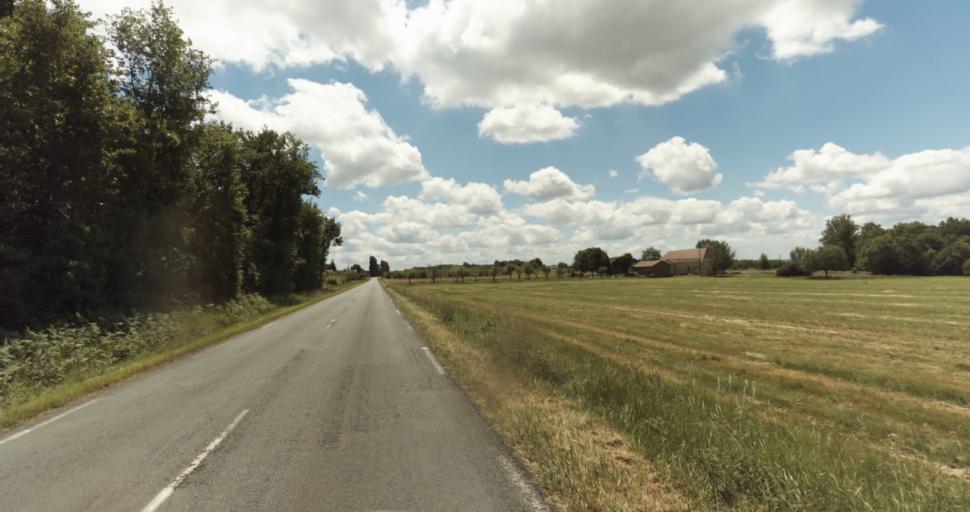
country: FR
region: Aquitaine
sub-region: Departement de la Dordogne
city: Beaumont-du-Perigord
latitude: 44.7443
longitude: 0.7805
